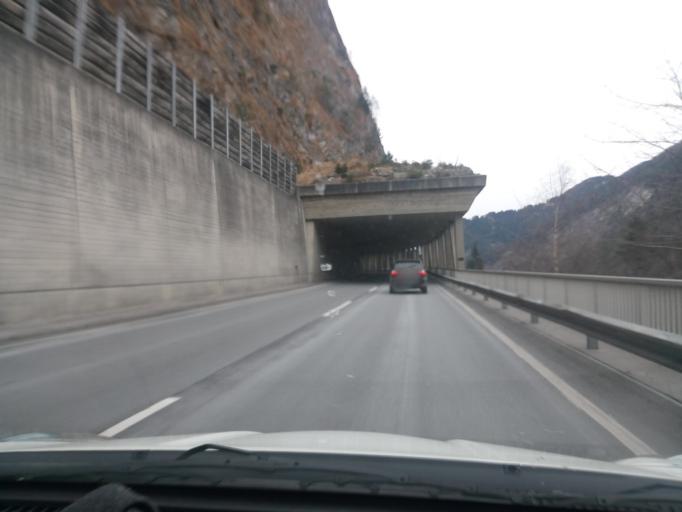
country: AT
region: Tyrol
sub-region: Politischer Bezirk Landeck
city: Nauders
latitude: 46.9256
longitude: 10.4914
